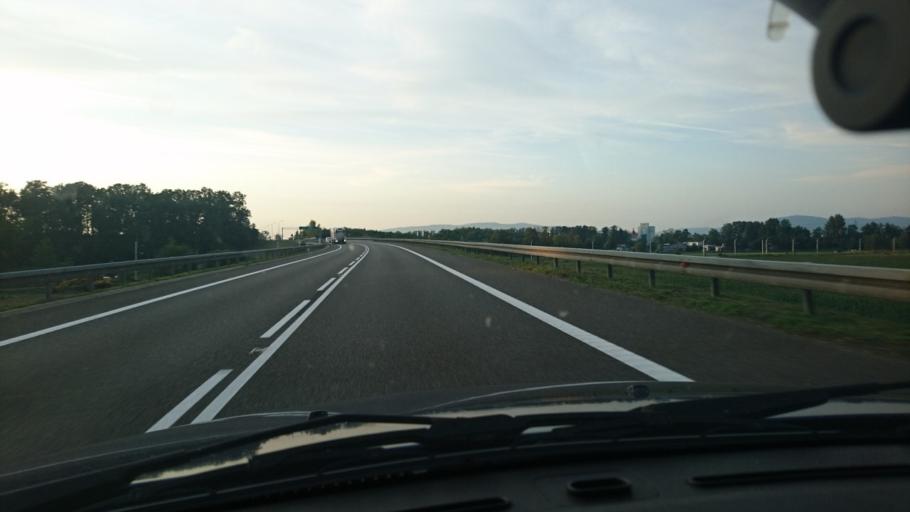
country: PL
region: Silesian Voivodeship
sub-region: Powiat zywiecki
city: Wieprz
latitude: 49.6536
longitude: 19.1703
